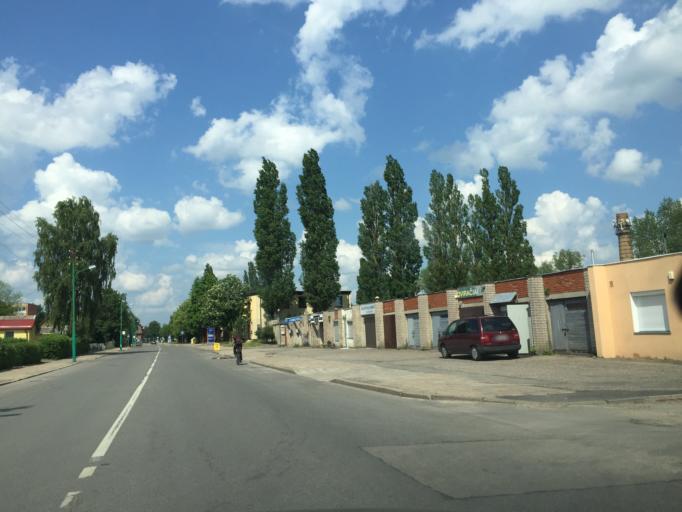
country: LT
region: Klaipedos apskritis
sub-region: Klaipeda
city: Palanga
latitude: 55.9224
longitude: 21.0739
